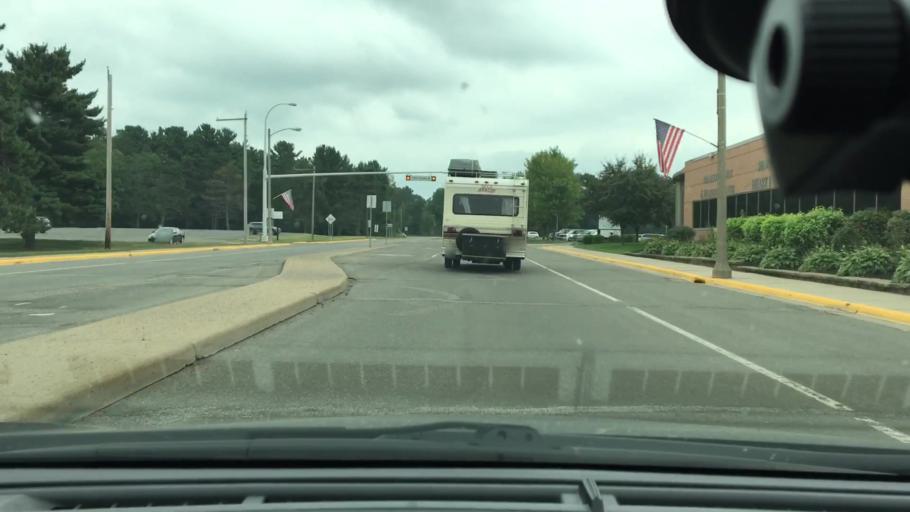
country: US
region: Minnesota
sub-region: Crow Wing County
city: Crosby
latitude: 46.4824
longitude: -93.9463
